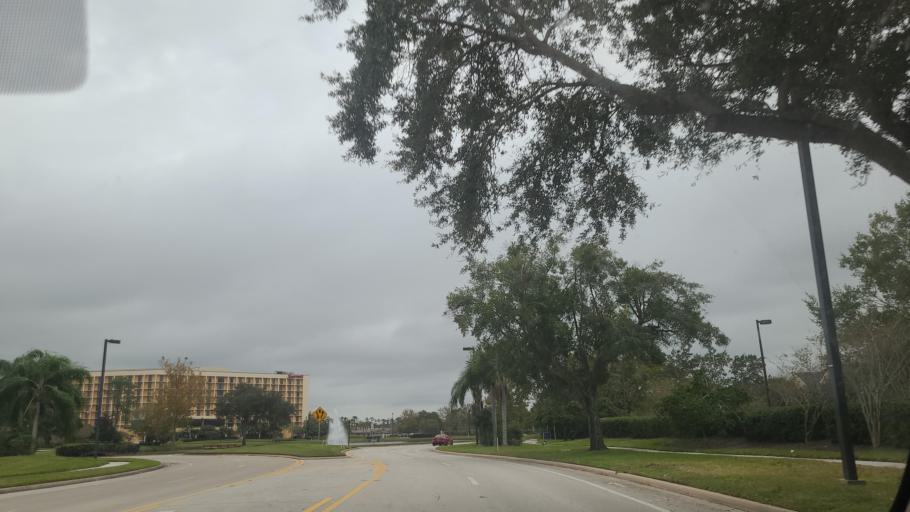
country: US
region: Florida
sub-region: Orange County
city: Conway
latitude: 28.4587
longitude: -81.3071
